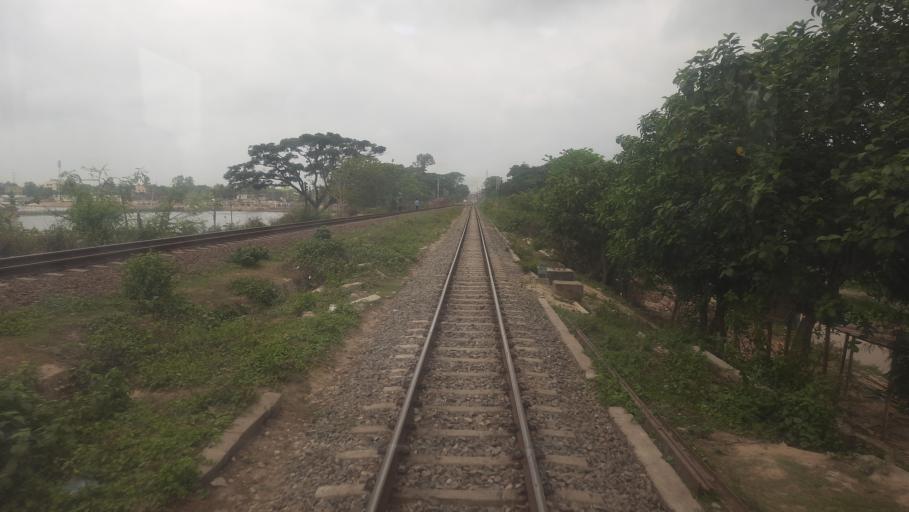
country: BD
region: Dhaka
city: Bhairab Bazar
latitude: 24.0505
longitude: 90.9845
